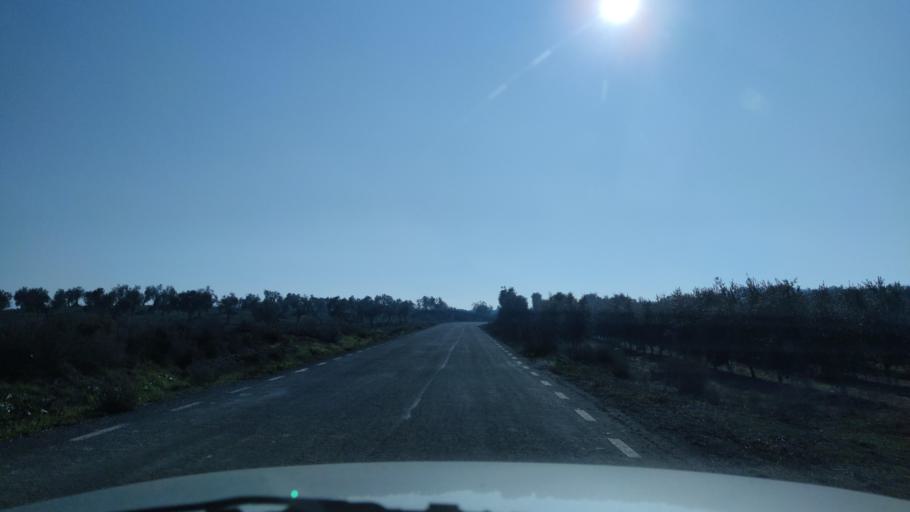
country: ES
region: Catalonia
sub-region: Provincia de Lleida
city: Torrebesses
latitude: 41.4493
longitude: 0.5585
